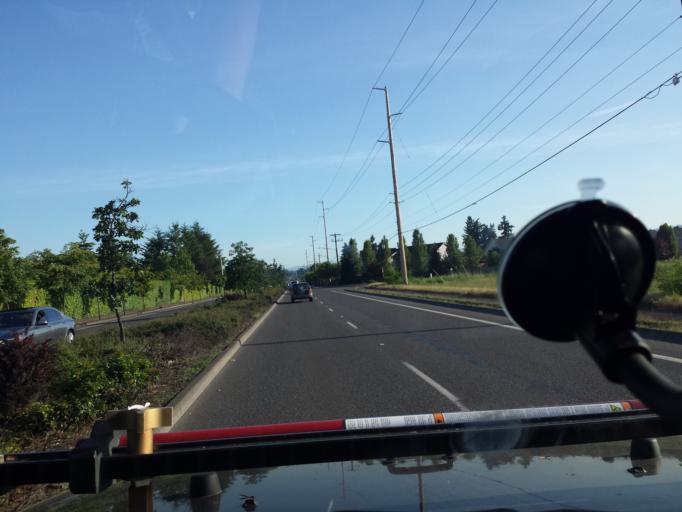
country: US
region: Washington
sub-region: Clark County
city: Mill Plain
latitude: 45.6517
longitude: -122.5060
